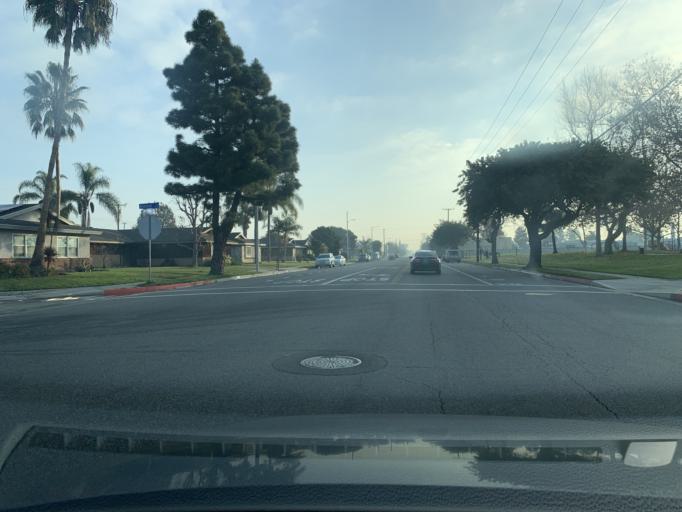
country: US
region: California
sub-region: Orange County
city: Westminster
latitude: 33.7372
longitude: -118.0397
